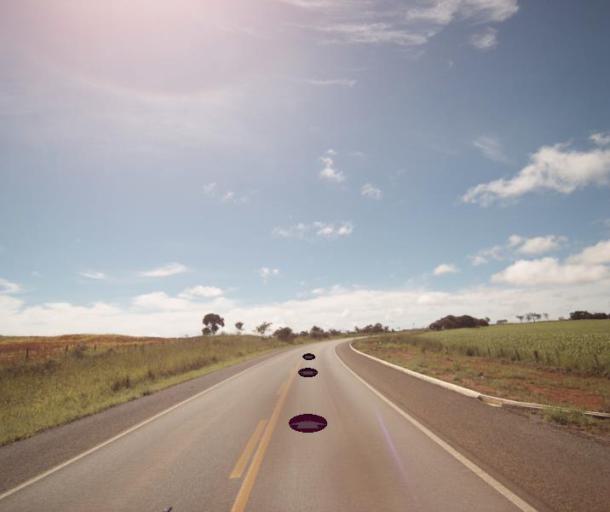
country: BR
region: Goias
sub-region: Padre Bernardo
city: Padre Bernardo
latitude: -15.2103
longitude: -48.4852
